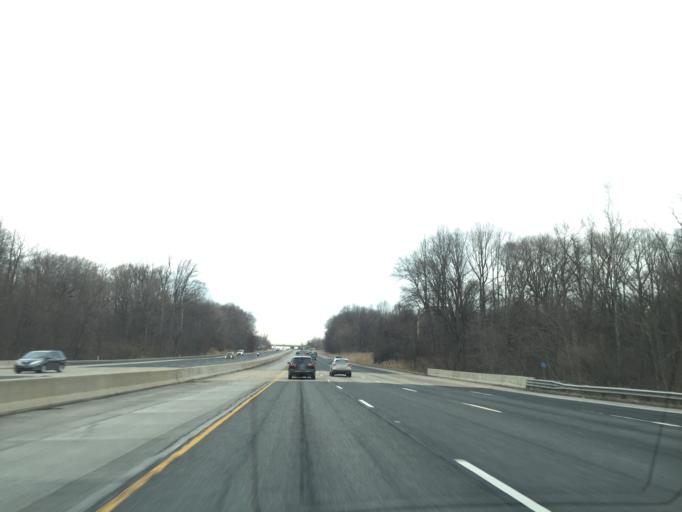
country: US
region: Indiana
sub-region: LaPorte County
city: Trail Creek
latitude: 41.6977
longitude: -86.8091
